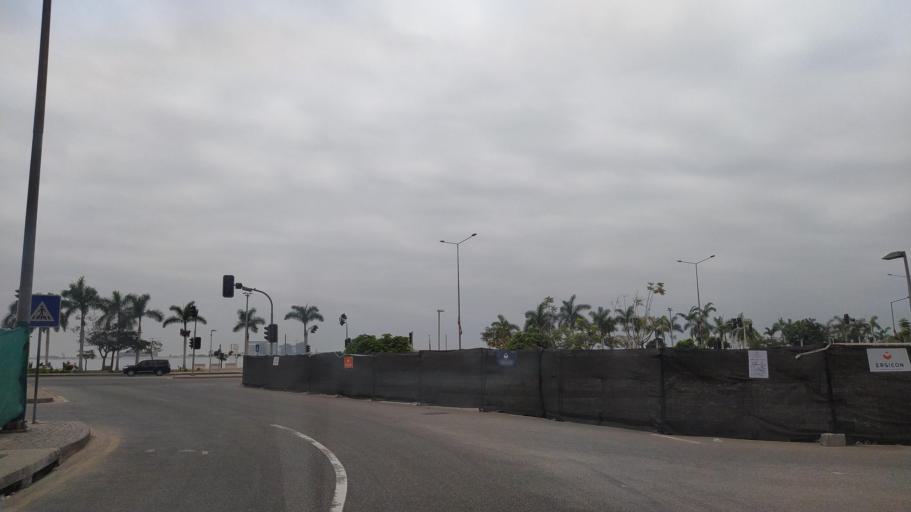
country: AO
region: Luanda
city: Luanda
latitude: -8.8103
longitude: 13.2354
